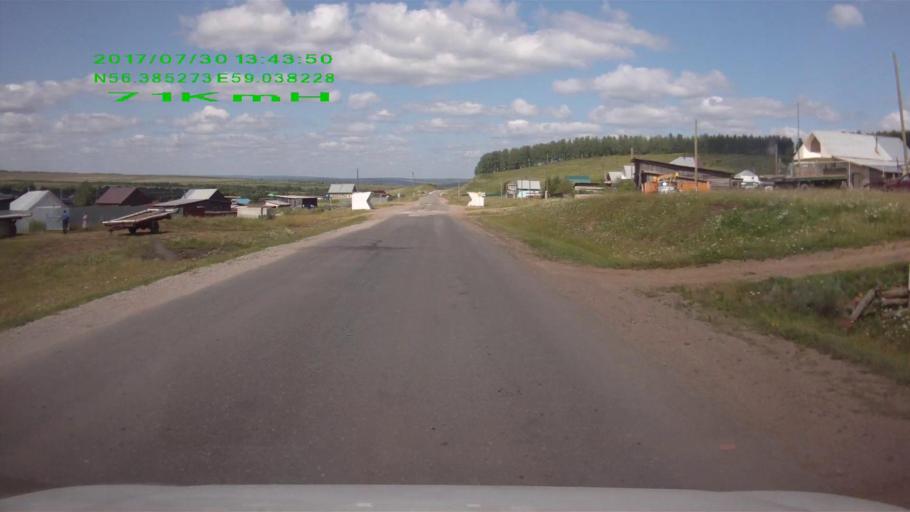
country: RU
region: Sverdlovsk
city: Mikhaylovsk
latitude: 56.3854
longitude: 59.0382
